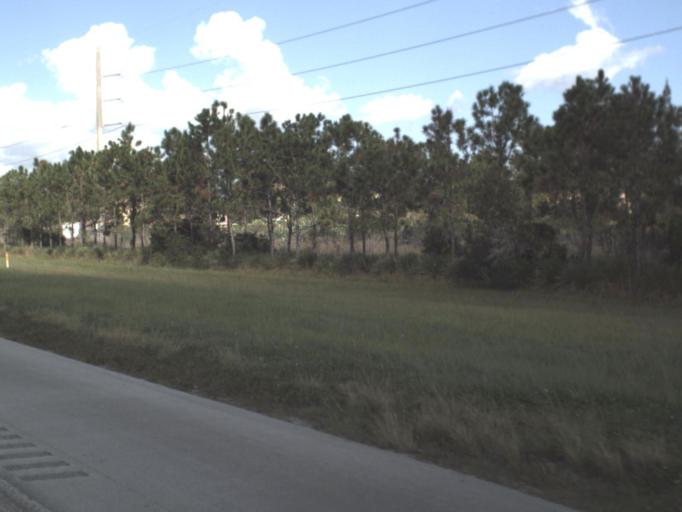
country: US
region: Florida
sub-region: Martin County
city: Palm City
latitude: 27.1510
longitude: -80.2975
